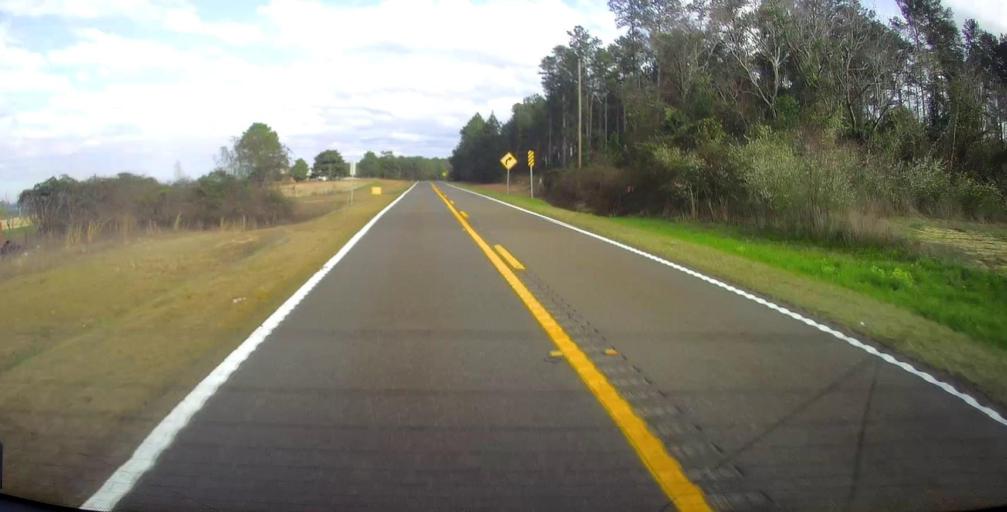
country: US
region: Georgia
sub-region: Marion County
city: Buena Vista
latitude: 32.4445
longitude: -84.5223
